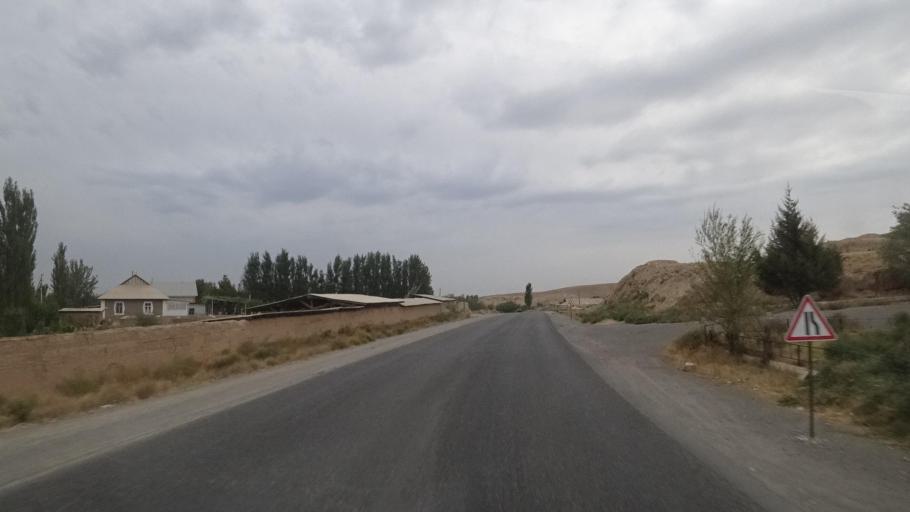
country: UZ
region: Namangan
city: Haqqulobod Shahri
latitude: 41.0622
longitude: 72.3350
